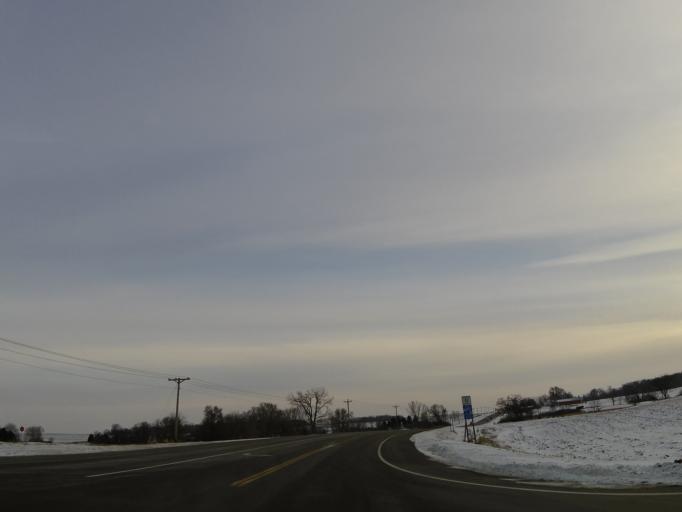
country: US
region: Minnesota
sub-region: Carver County
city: Carver
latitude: 44.7912
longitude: -93.6425
